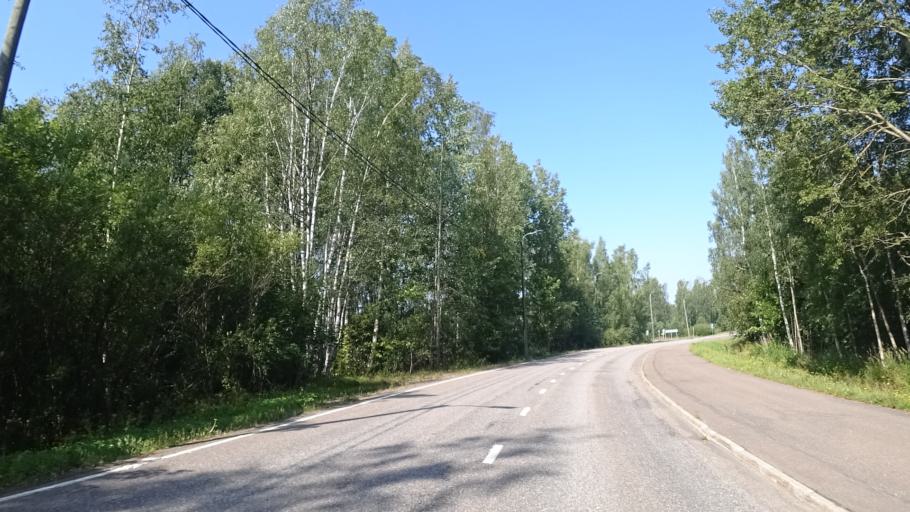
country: FI
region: Kymenlaakso
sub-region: Kotka-Hamina
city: Karhula
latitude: 60.5048
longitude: 26.9474
